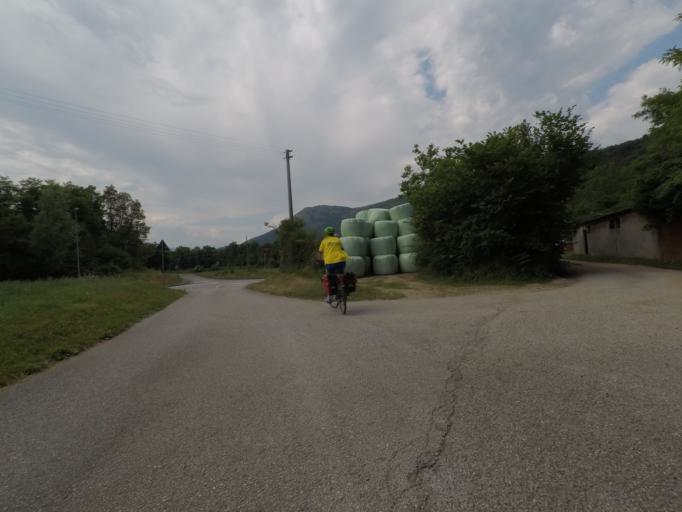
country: IT
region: Friuli Venezia Giulia
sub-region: Provincia di Pordenone
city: Travesio
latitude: 46.1895
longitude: 12.8790
